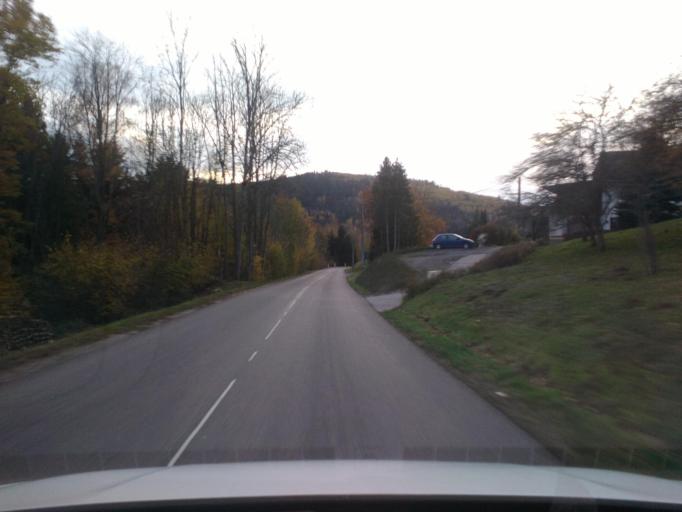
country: FR
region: Lorraine
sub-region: Departement des Vosges
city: Plainfaing
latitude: 48.1864
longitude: 7.0182
